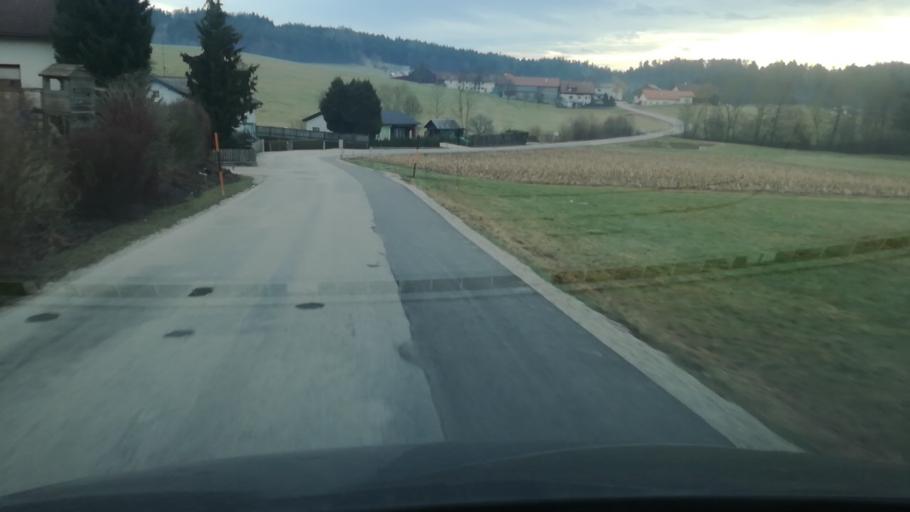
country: AT
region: Upper Austria
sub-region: Politischer Bezirk Vocklabruck
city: Frankenburg
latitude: 48.0614
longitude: 13.5099
